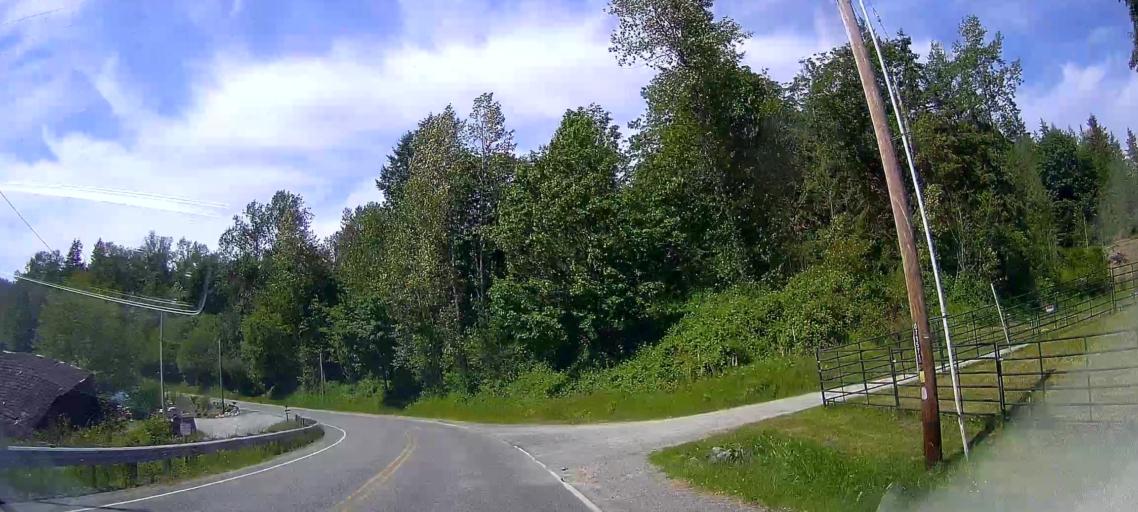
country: US
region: Washington
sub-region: Skagit County
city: Big Lake
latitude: 48.3961
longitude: -122.2866
